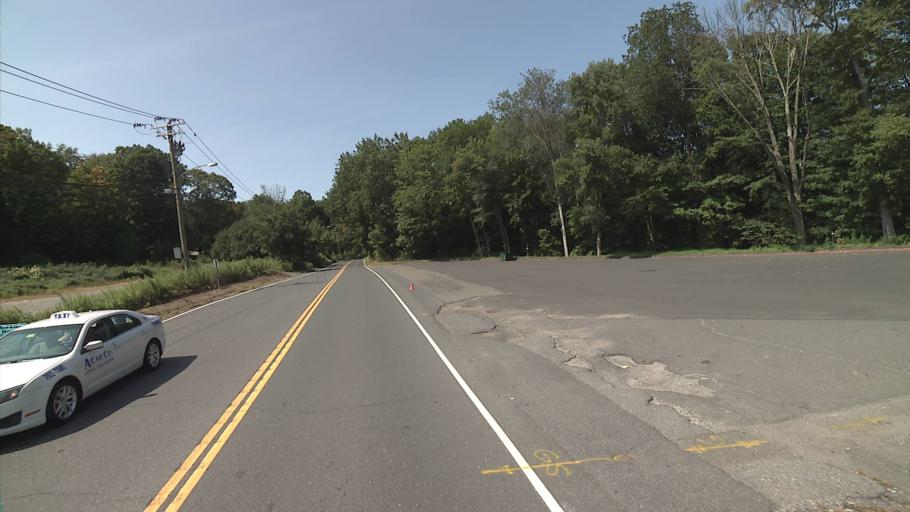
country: US
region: Connecticut
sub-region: Fairfield County
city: Fairfield
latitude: 41.2037
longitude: -73.2719
